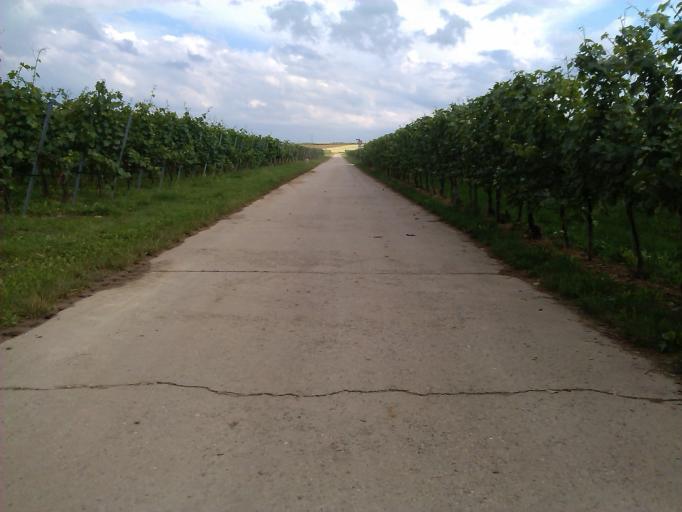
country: DE
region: Baden-Wuerttemberg
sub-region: Regierungsbezirk Stuttgart
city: Lauffen am Neckar
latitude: 49.0652
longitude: 9.1651
